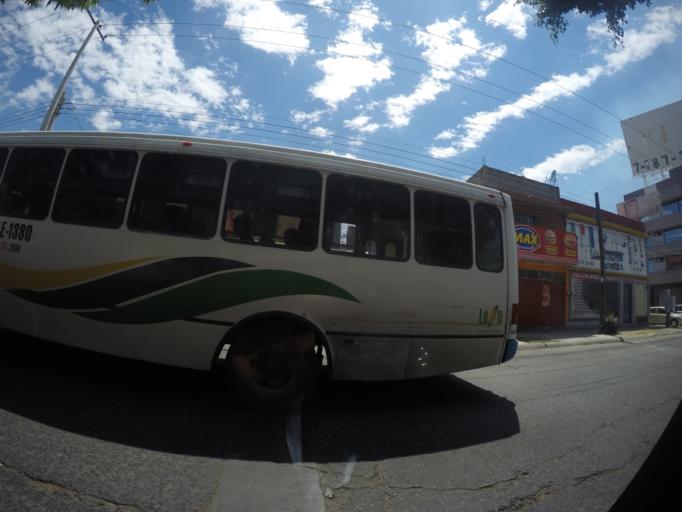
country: MX
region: Guanajuato
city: Leon
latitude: 21.1046
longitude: -101.6490
